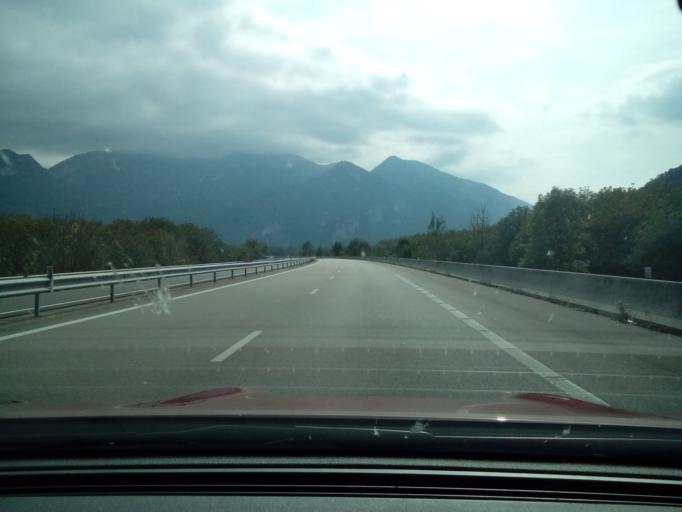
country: FR
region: Rhone-Alpes
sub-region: Departement de l'Isere
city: Tullins
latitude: 45.2294
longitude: 5.4824
